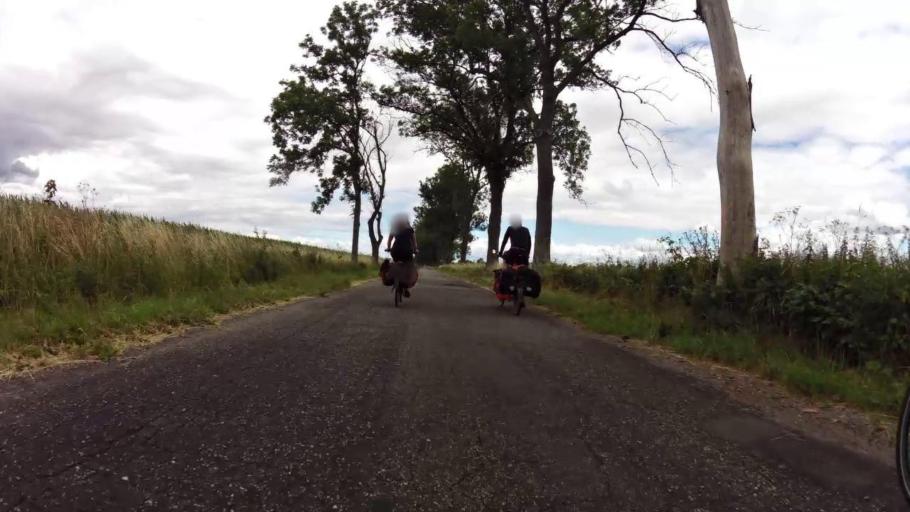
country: PL
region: West Pomeranian Voivodeship
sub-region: Powiat lobeski
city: Lobez
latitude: 53.7588
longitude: 15.5737
